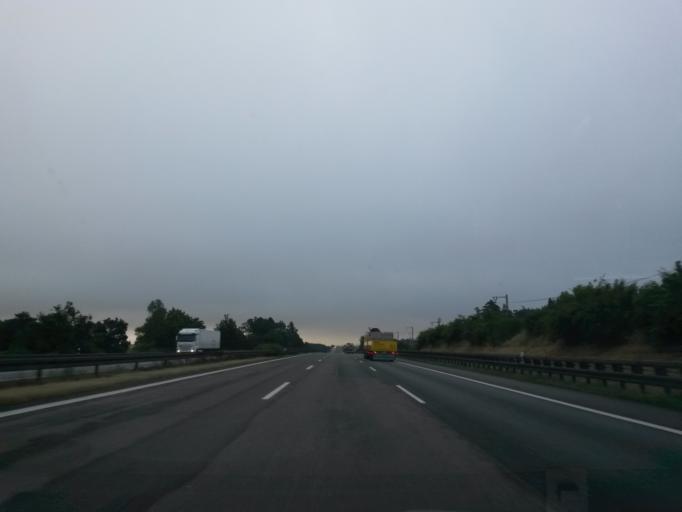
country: DE
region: Bavaria
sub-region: Regierungsbezirk Mittelfranken
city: Hilpoltstein
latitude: 49.1990
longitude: 11.2415
